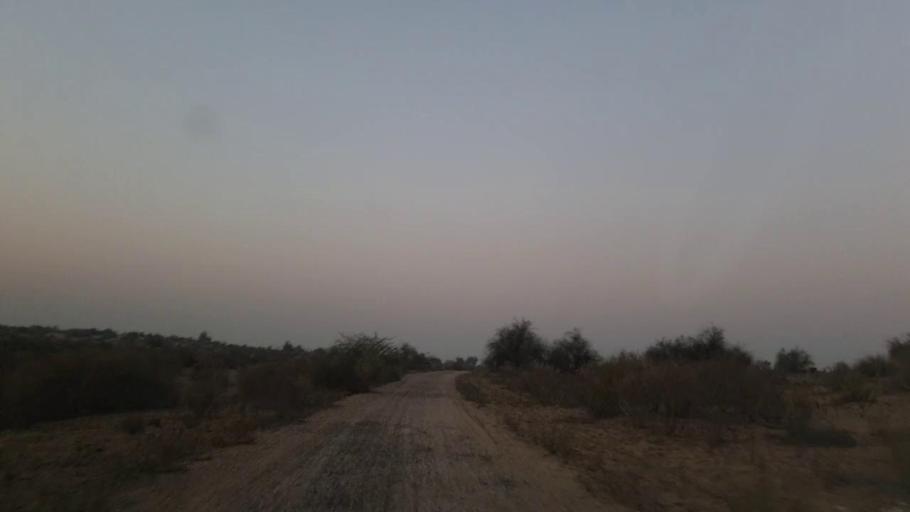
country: PK
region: Sindh
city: Bandhi
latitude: 26.6114
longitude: 68.3896
